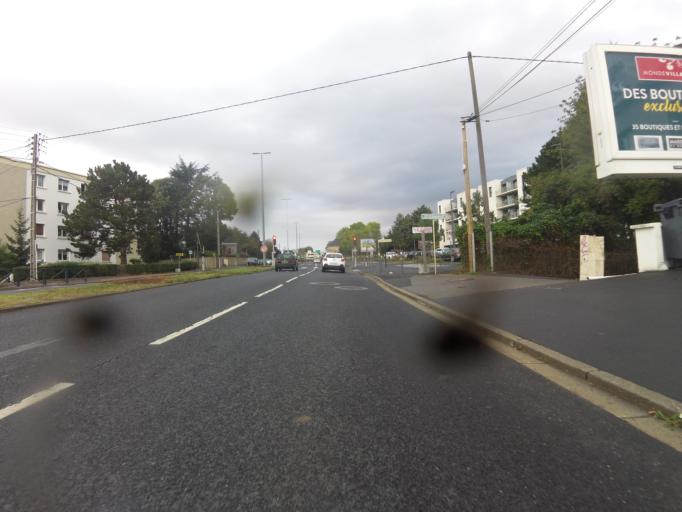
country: FR
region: Lower Normandy
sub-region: Departement du Calvados
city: Saint-Germain-la-Blanche-Herbe
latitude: 49.1808
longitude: -0.3879
